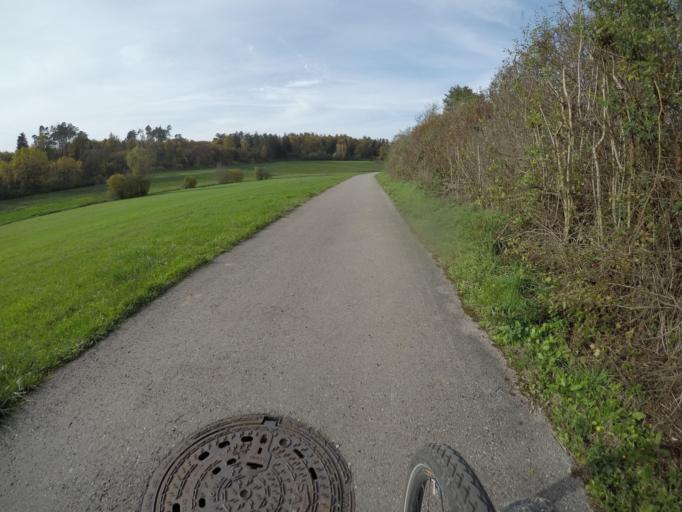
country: DE
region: Baden-Wuerttemberg
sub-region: Regierungsbezirk Stuttgart
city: Weil der Stadt
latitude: 48.7700
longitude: 8.8930
